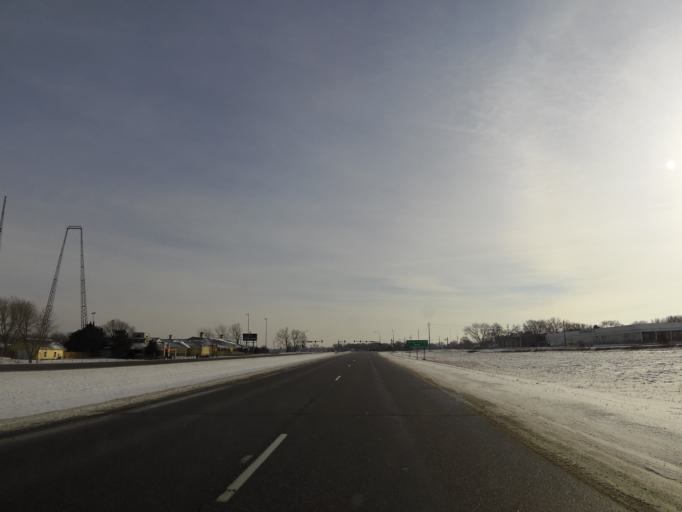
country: US
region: Minnesota
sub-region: Hennepin County
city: Eden Prairie
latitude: 44.7968
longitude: -93.4540
